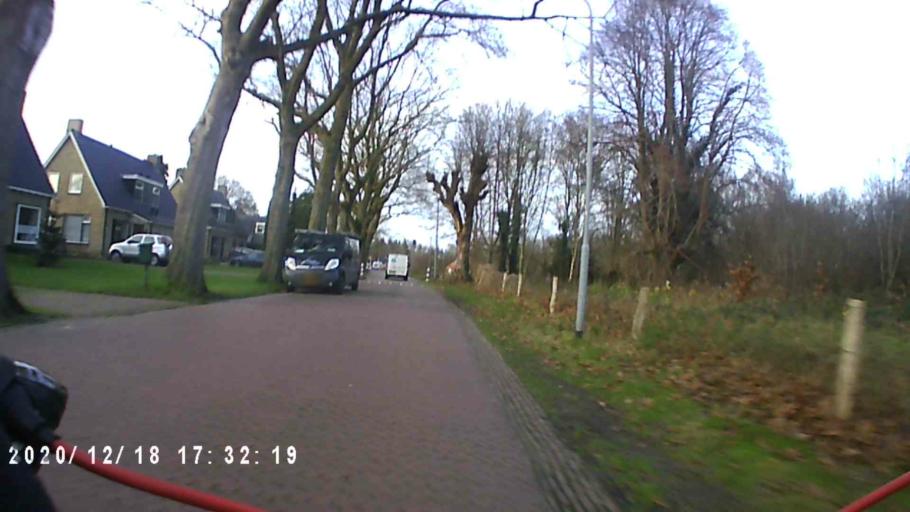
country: NL
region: Drenthe
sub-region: Gemeente Tynaarlo
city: Vries
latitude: 53.0808
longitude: 6.5749
